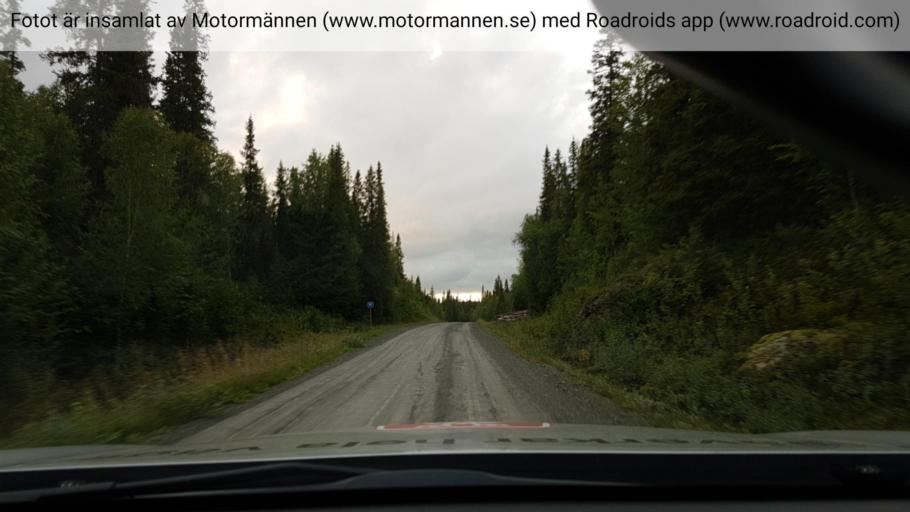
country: SE
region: Vaesterbotten
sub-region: Vilhelmina Kommun
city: Sjoberg
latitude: 65.5064
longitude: 15.4741
